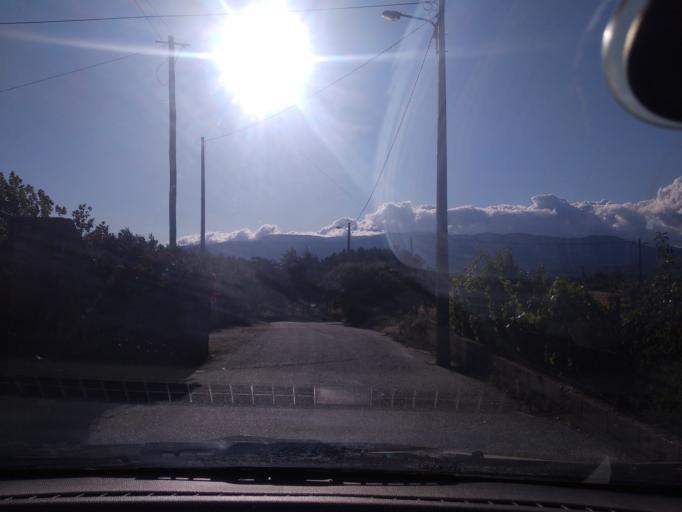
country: PT
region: Castelo Branco
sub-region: Covilha
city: Teixoso
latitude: 40.2578
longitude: -7.3932
